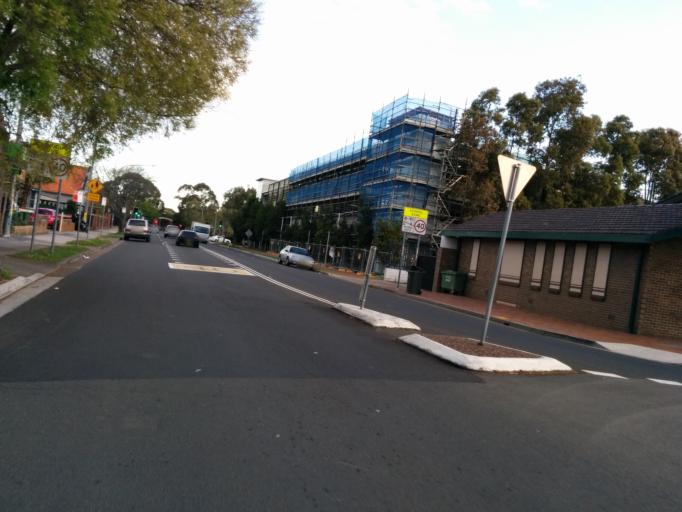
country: AU
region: New South Wales
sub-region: Fairfield
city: Carramar
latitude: -33.8719
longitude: 150.9585
